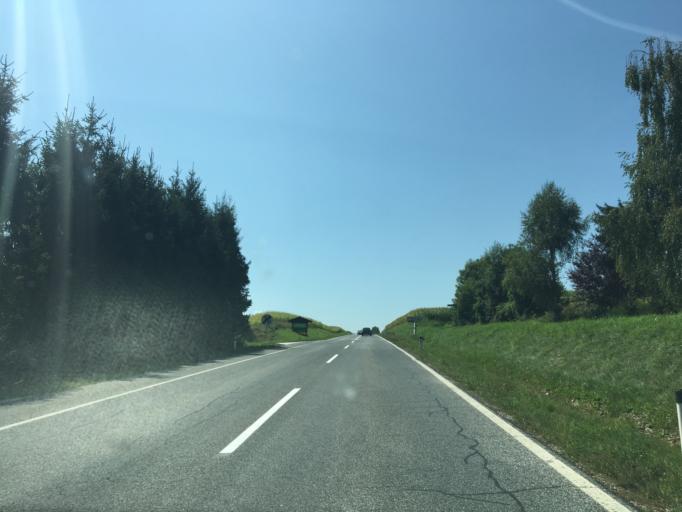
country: AT
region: Carinthia
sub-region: Politischer Bezirk Volkermarkt
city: Griffen
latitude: 46.6997
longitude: 14.7216
